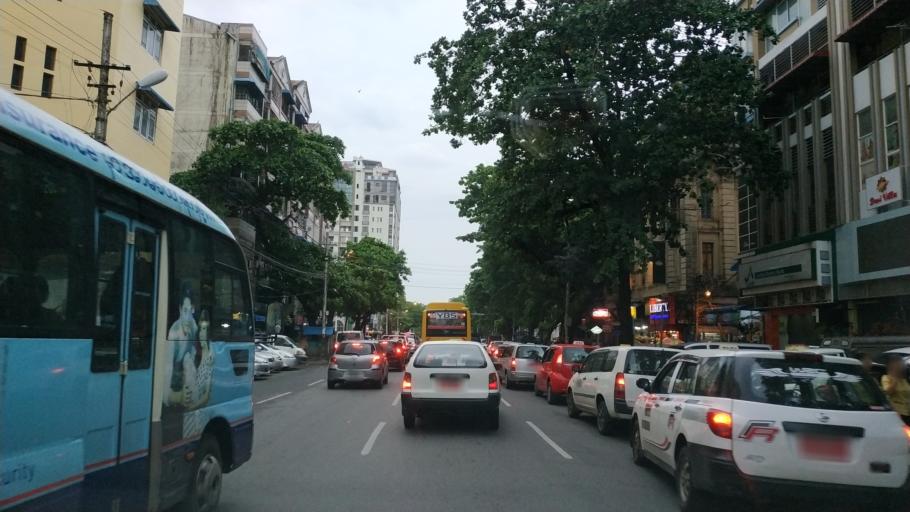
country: MM
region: Yangon
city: Yangon
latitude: 16.7719
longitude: 96.1567
